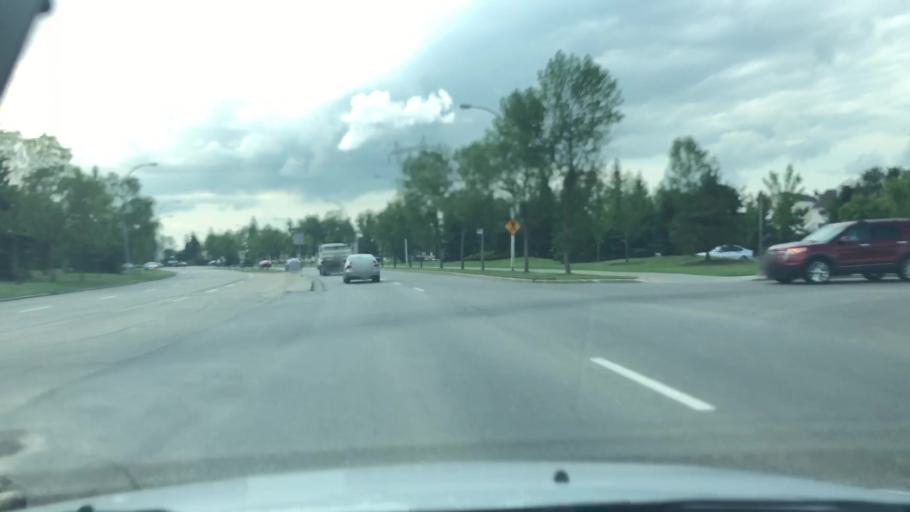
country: CA
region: Alberta
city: Edmonton
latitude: 53.6161
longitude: -113.5267
